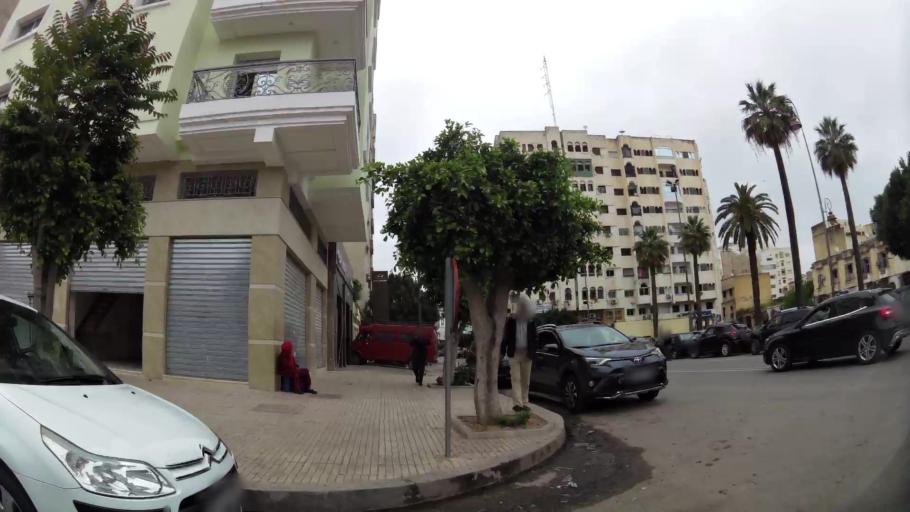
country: MA
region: Fes-Boulemane
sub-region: Fes
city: Fes
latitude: 34.0398
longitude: -4.9980
